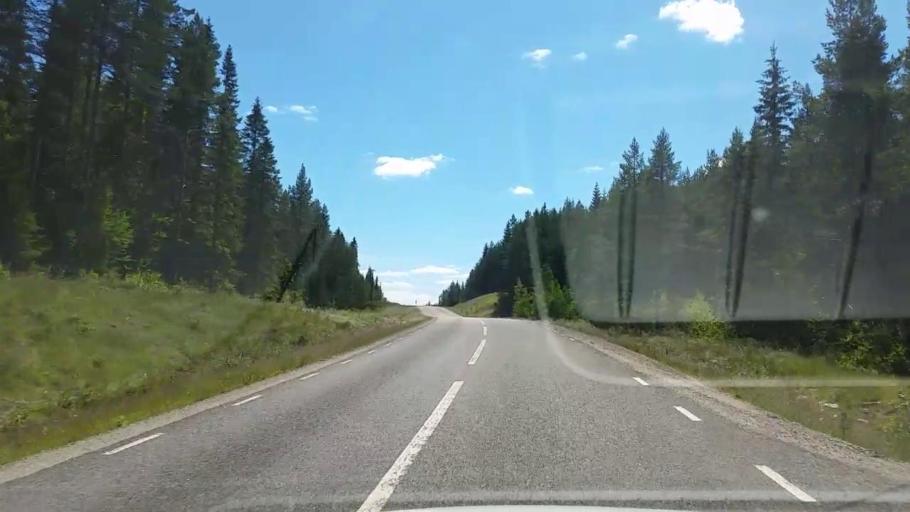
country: SE
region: Gaevleborg
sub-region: Ovanakers Kommun
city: Edsbyn
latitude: 61.5226
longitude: 15.6786
